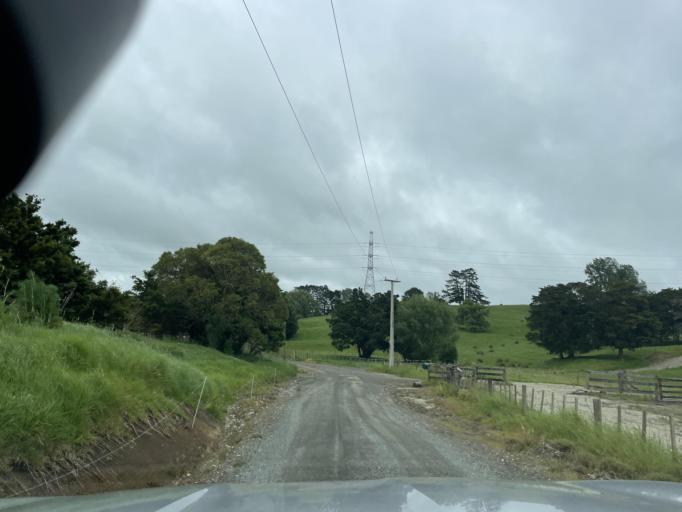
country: NZ
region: Northland
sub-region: Whangarei
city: Ruakaka
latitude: -36.0976
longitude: 174.4167
